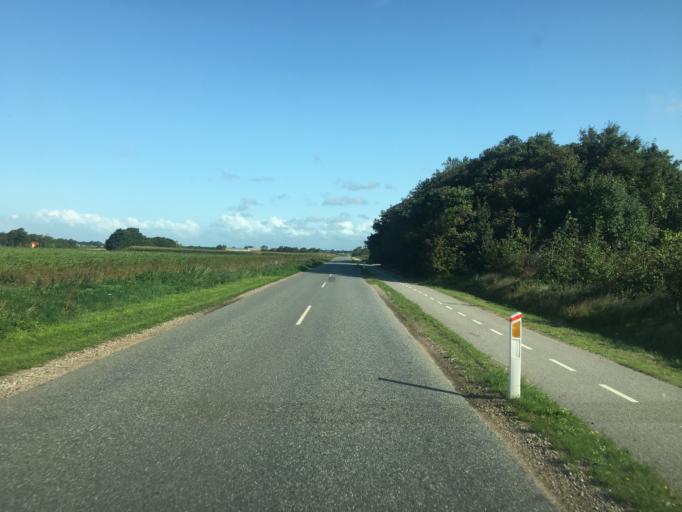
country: DK
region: South Denmark
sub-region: Tonder Kommune
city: Sherrebek
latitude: 55.1338
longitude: 8.7613
